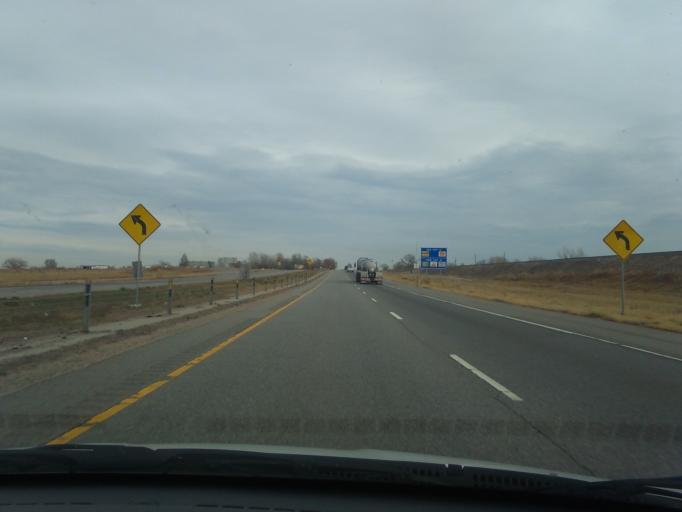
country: US
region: Colorado
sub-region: Weld County
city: Hudson
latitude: 40.0620
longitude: -104.6543
